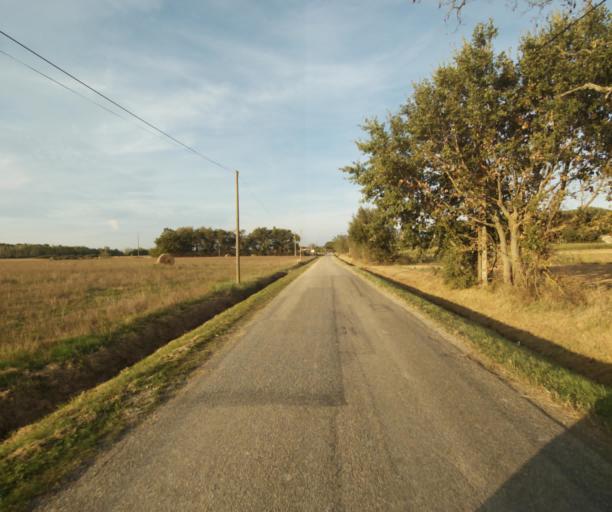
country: FR
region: Midi-Pyrenees
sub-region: Departement du Tarn-et-Garonne
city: Campsas
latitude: 43.8900
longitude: 1.3554
